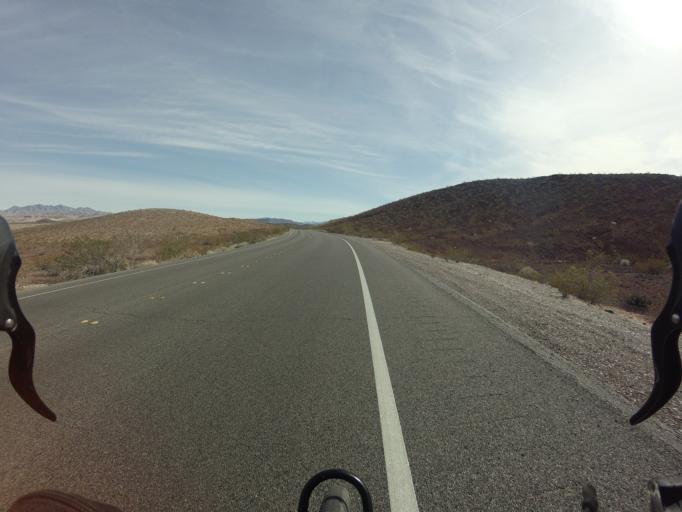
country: US
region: Nevada
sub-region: Clark County
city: Henderson
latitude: 36.1456
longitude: -114.8811
